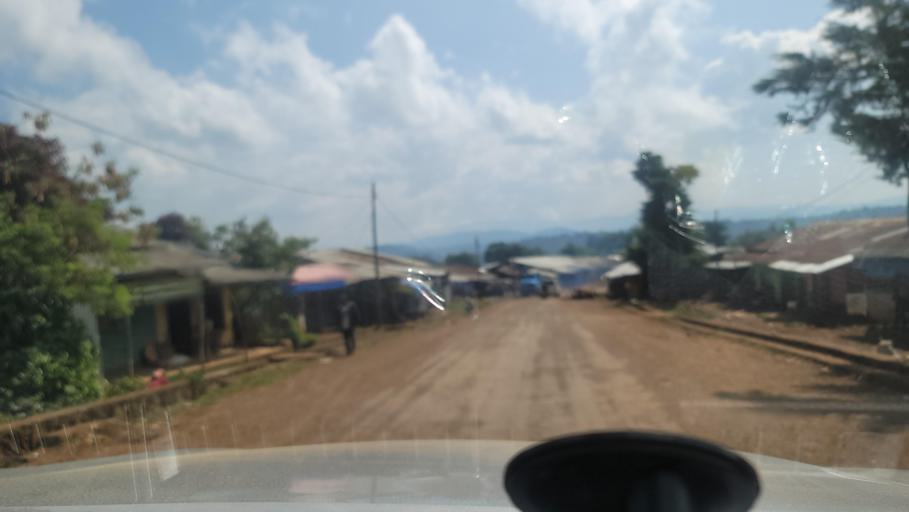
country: ET
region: Oromiya
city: Agaro
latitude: 7.7403
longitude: 36.2524
